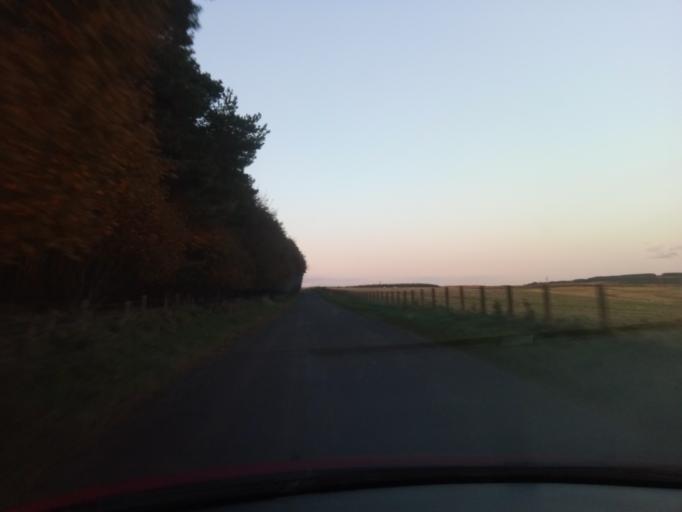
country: GB
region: Scotland
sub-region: East Lothian
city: Pencaitland
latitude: 55.8133
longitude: -2.8757
